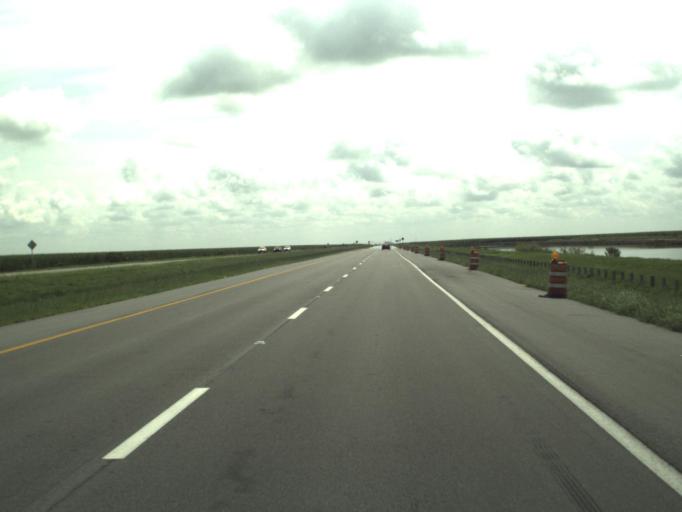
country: US
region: Florida
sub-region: Palm Beach County
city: Belle Glade
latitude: 26.7262
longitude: -80.6338
